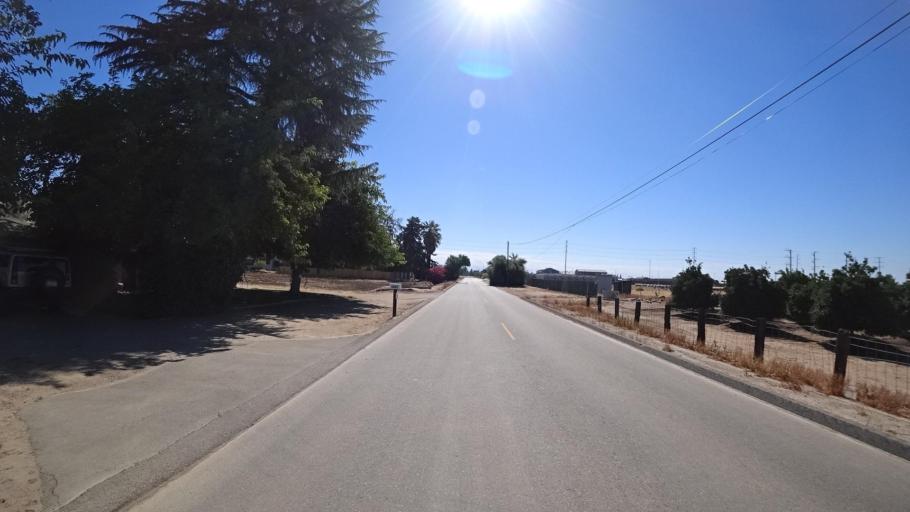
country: US
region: California
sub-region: Fresno County
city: Sunnyside
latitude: 36.7612
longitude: -119.6802
